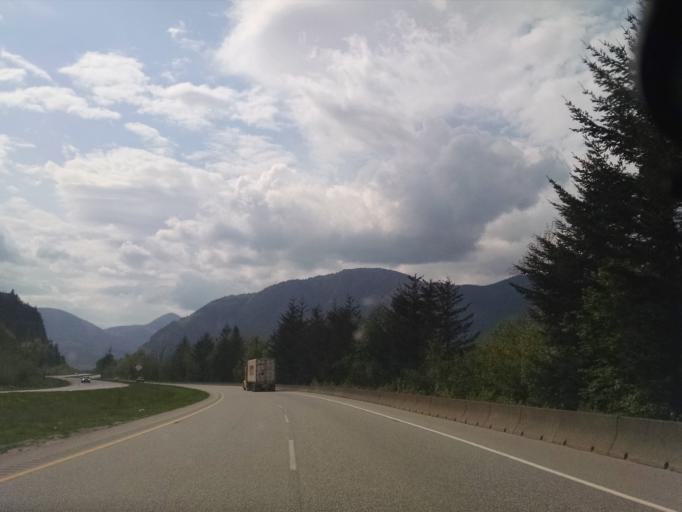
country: CA
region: British Columbia
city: Hope
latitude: 49.3643
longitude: -121.5451
